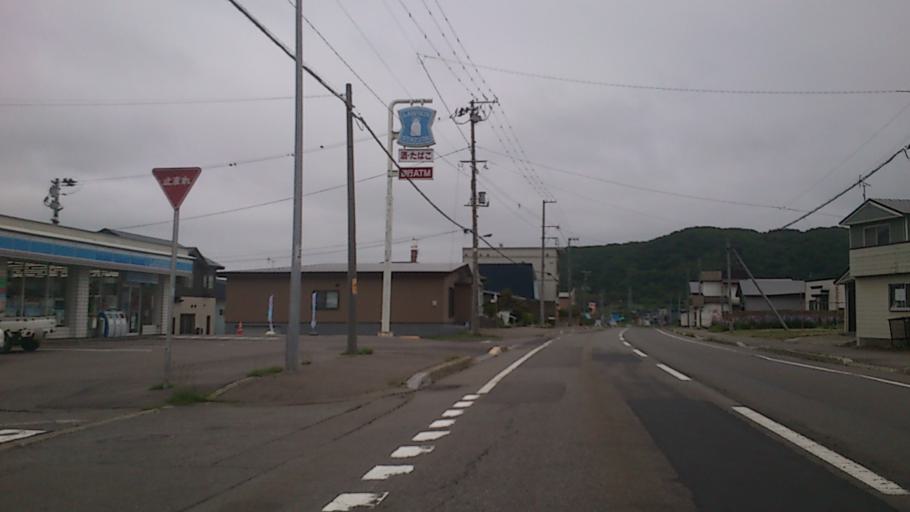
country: JP
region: Hokkaido
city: Kamiiso
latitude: 41.9764
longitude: 140.1357
